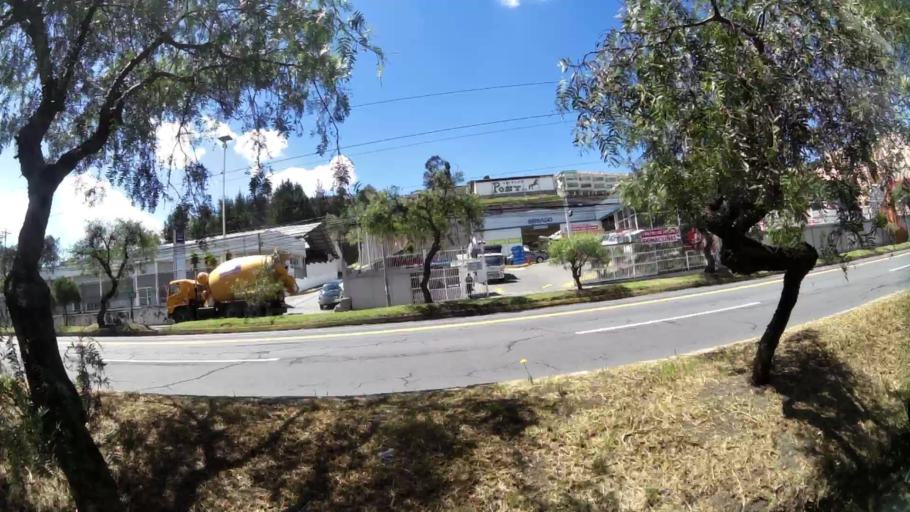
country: EC
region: Pichincha
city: Quito
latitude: -0.1184
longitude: -78.4799
